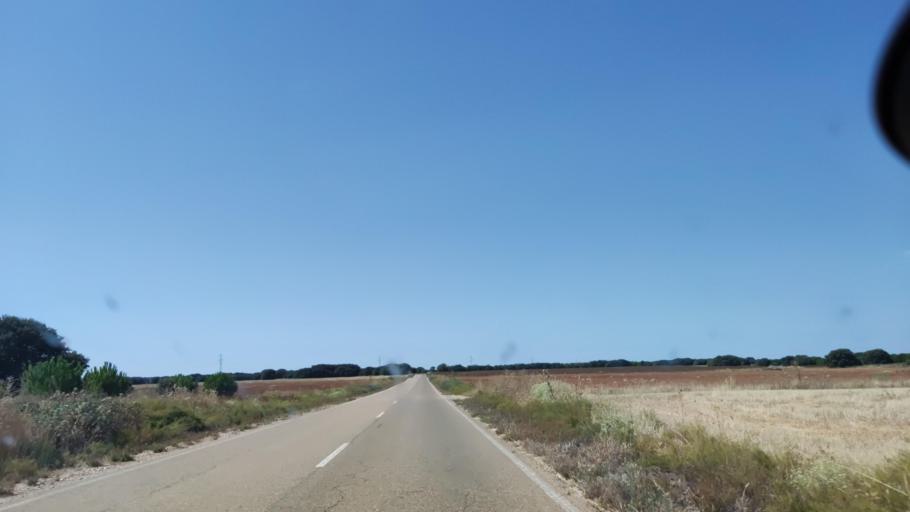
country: ES
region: Castille and Leon
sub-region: Provincia de Valladolid
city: Uruena
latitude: 41.7065
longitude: -5.1997
